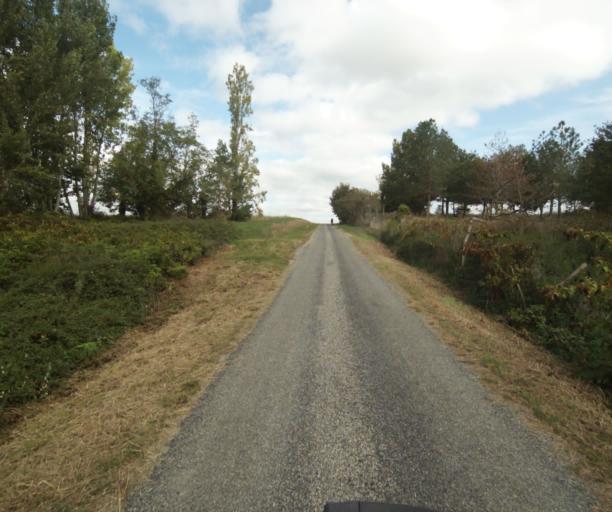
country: FR
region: Midi-Pyrenees
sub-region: Departement du Tarn-et-Garonne
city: Finhan
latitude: 43.9290
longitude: 1.2147
